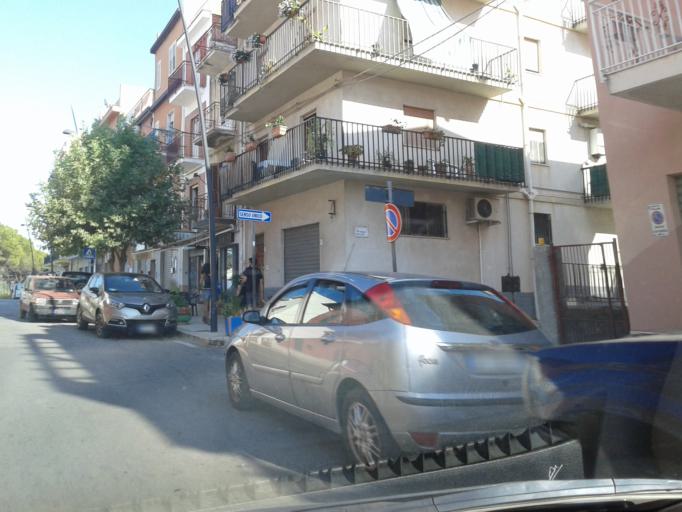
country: IT
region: Sicily
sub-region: Palermo
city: Finale
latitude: 38.0199
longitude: 14.1631
